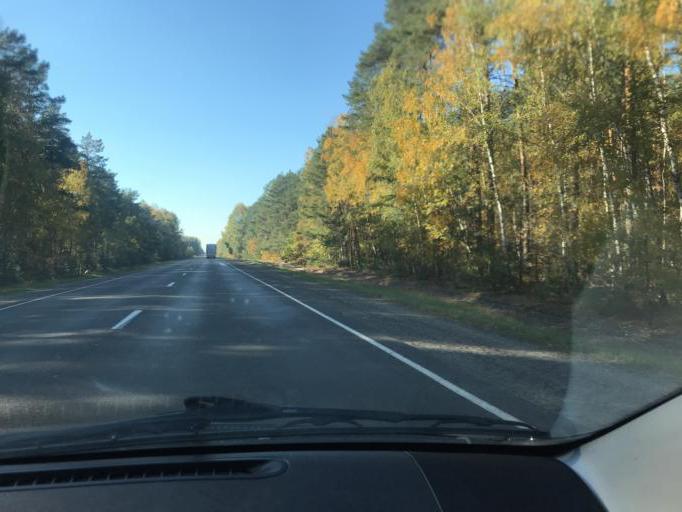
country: BY
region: Brest
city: Davyd-Haradok
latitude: 52.2386
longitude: 27.2829
